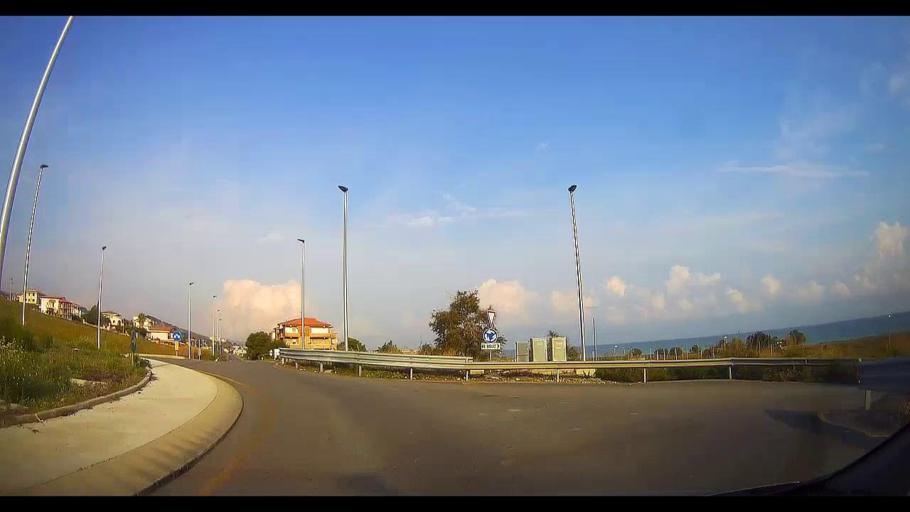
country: IT
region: Calabria
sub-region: Provincia di Cosenza
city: Cariati
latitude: 39.5235
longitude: 16.8965
